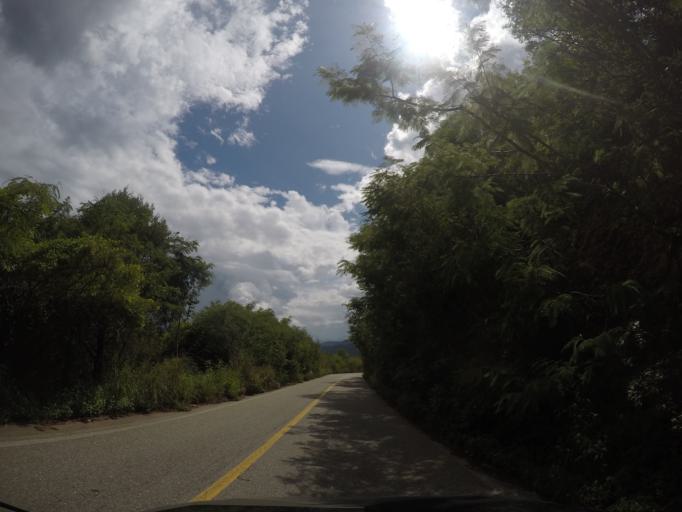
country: MX
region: Oaxaca
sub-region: San Jeronimo Coatlan
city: San Cristobal Honduras
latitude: 16.4344
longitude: -97.0508
